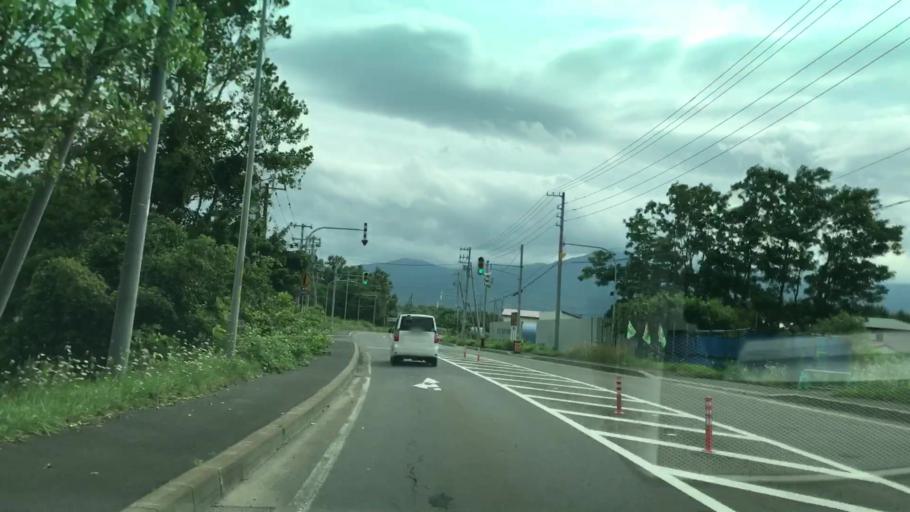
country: JP
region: Hokkaido
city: Iwanai
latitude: 43.0072
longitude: 140.5426
